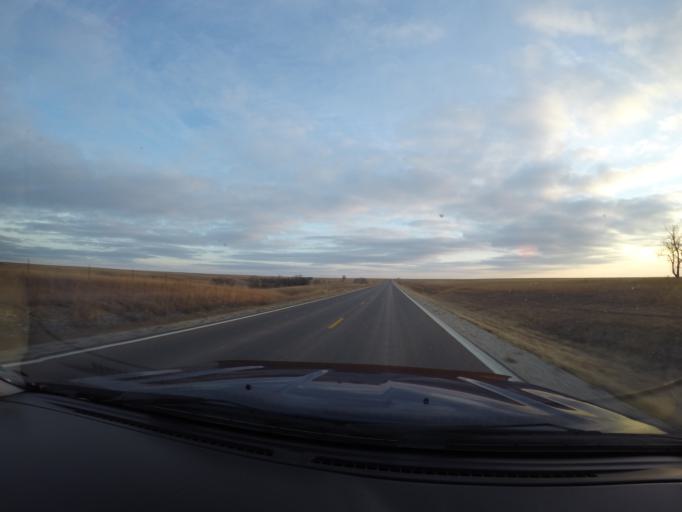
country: US
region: Kansas
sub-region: Morris County
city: Council Grove
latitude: 38.5589
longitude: -96.5220
